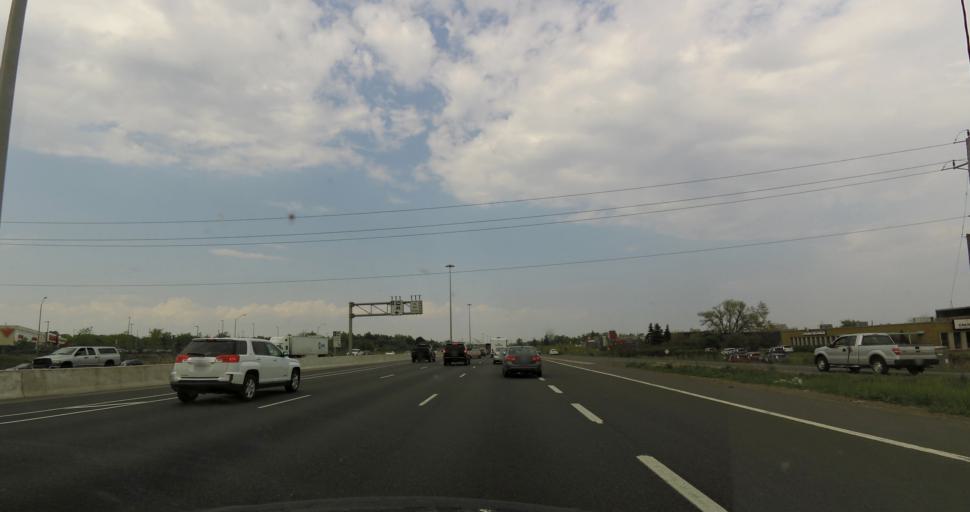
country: CA
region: Ontario
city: Oakville
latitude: 43.4478
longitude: -79.6983
